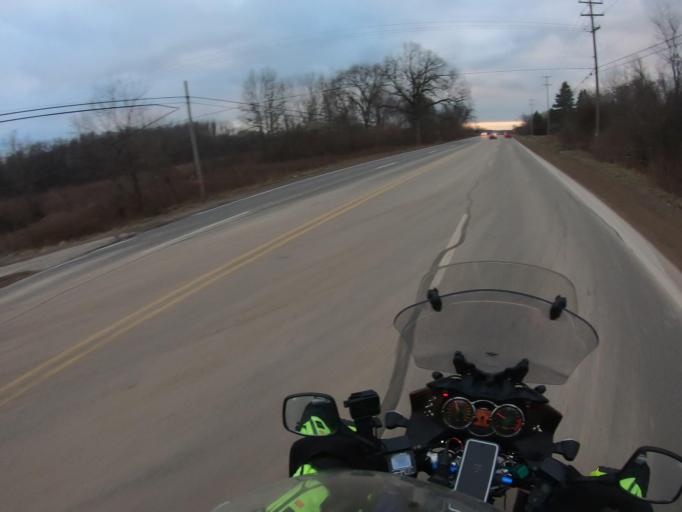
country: US
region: Michigan
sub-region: Genesee County
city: Grand Blanc
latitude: 42.8618
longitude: -83.5816
